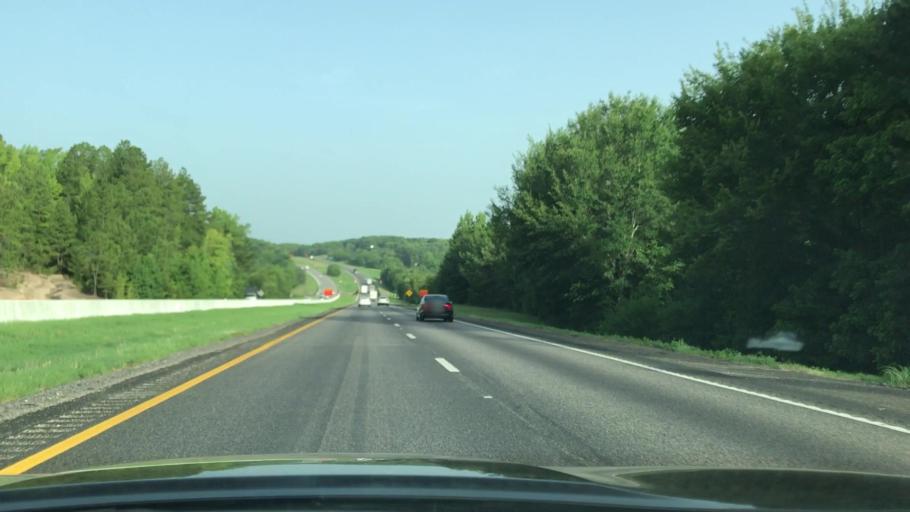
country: US
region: Texas
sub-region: Smith County
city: Lindale
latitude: 32.4657
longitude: -95.3356
